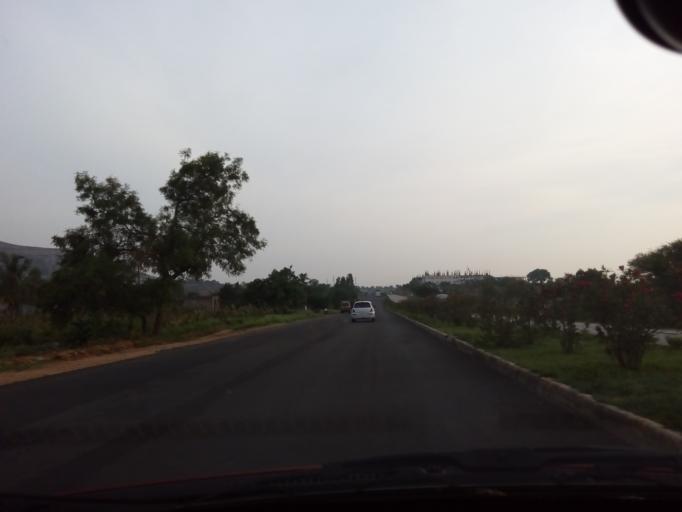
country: IN
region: Karnataka
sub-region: Chikkaballapur
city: Gudibanda
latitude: 13.6178
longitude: 77.7900
